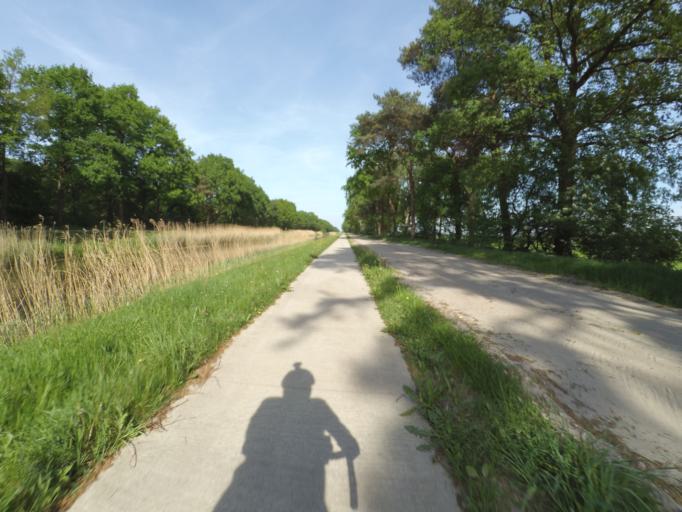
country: NL
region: Overijssel
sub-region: Gemeente Tubbergen
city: Tubbergen
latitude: 52.3745
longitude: 6.8652
